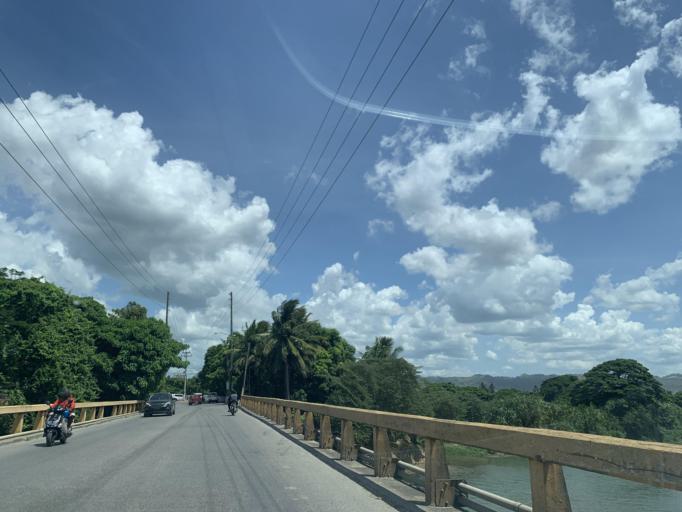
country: DO
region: Espaillat
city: Jamao al Norte
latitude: 19.6729
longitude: -70.3730
